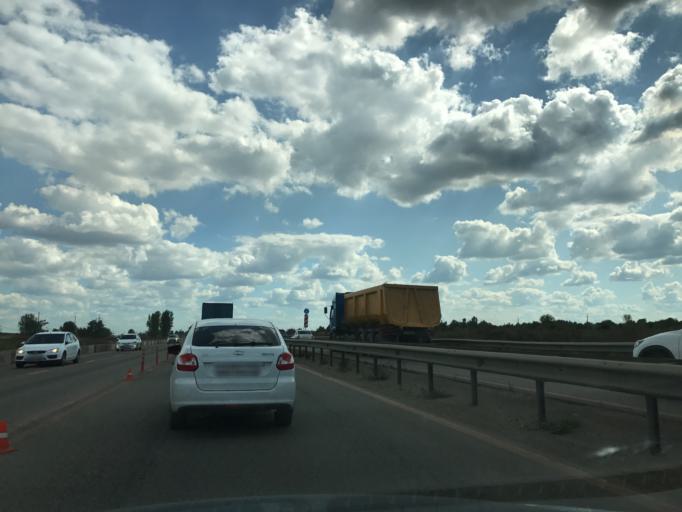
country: RU
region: Adygeya
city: Tlyustenkhabl'
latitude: 44.9486
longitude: 39.1248
